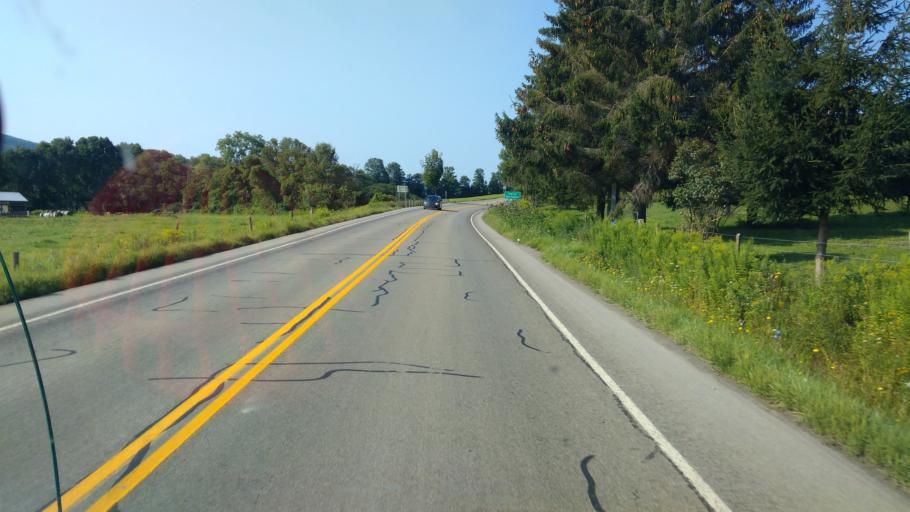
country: US
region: New York
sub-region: Allegany County
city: Friendship
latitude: 42.2972
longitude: -78.1914
